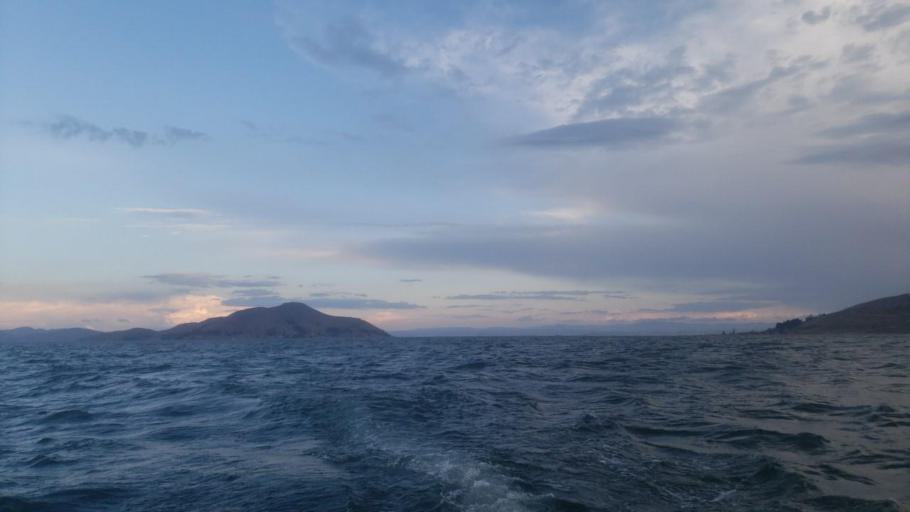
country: BO
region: La Paz
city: San Pedro
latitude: -16.2614
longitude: -68.8060
